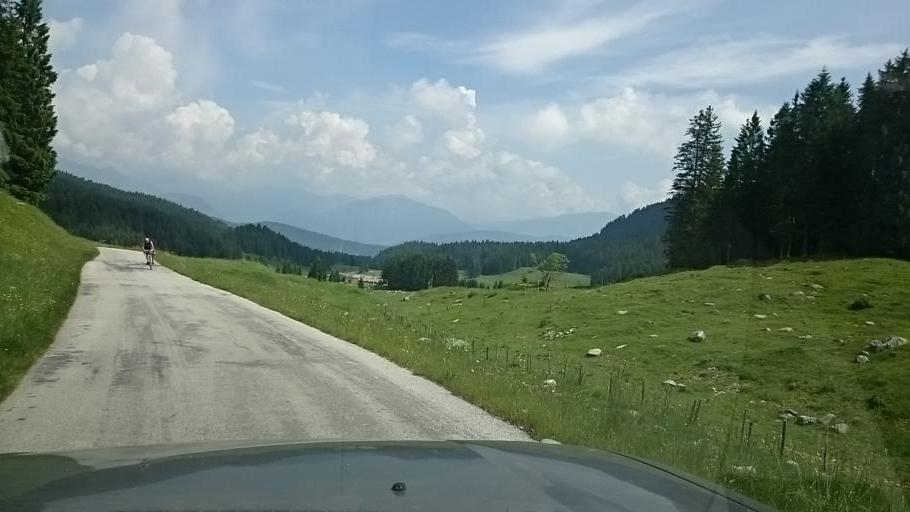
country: IT
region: Trentino-Alto Adige
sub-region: Provincia di Trento
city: Grigno
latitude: 45.9786
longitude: 11.5957
